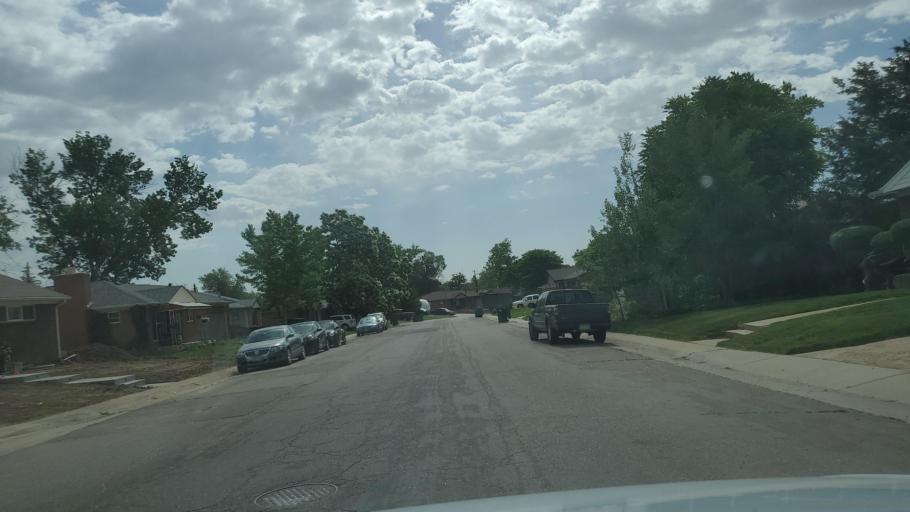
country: US
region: Colorado
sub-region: Adams County
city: Twin Lakes
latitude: 39.8308
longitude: -105.0127
